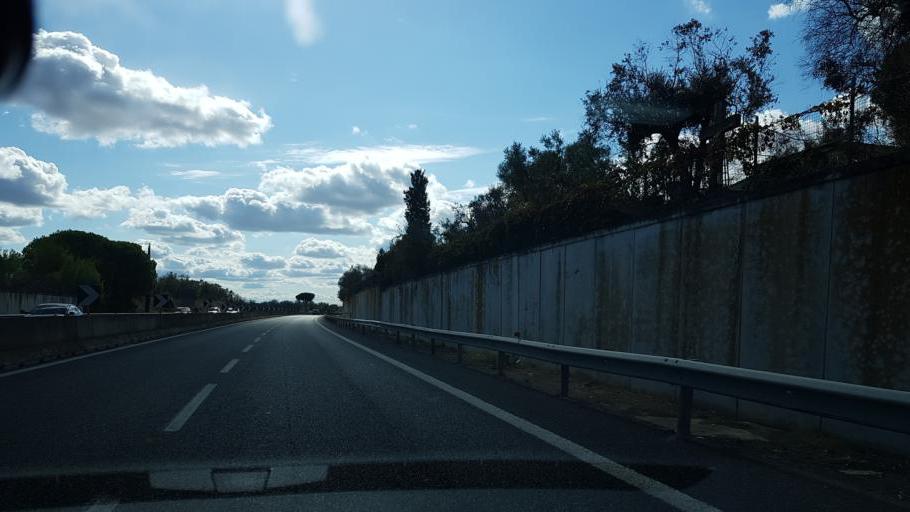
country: IT
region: Apulia
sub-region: Provincia di Brindisi
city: Torchiarolo
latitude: 40.4622
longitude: 18.0584
